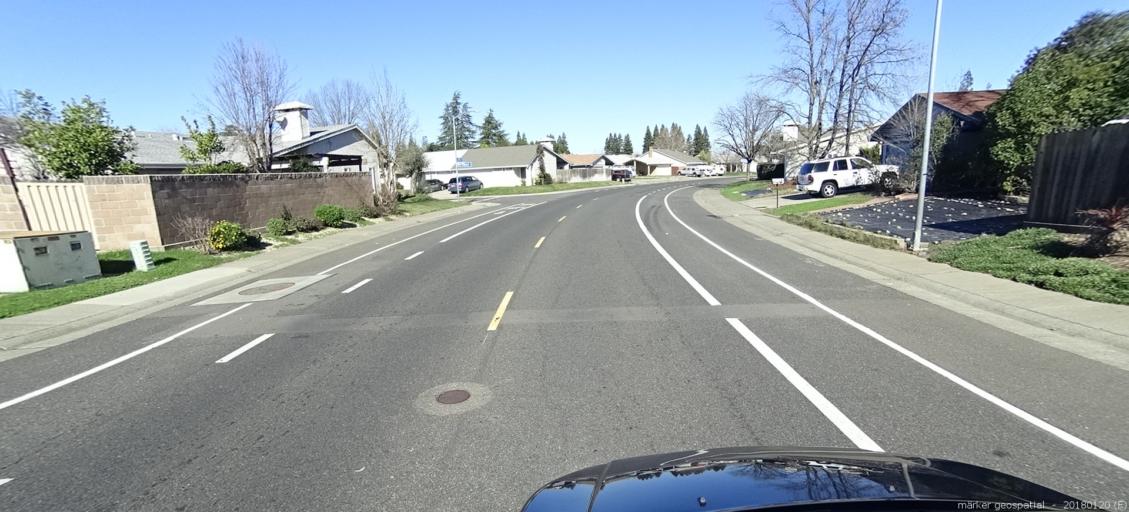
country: US
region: California
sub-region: Sacramento County
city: La Riviera
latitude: 38.5656
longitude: -121.3333
